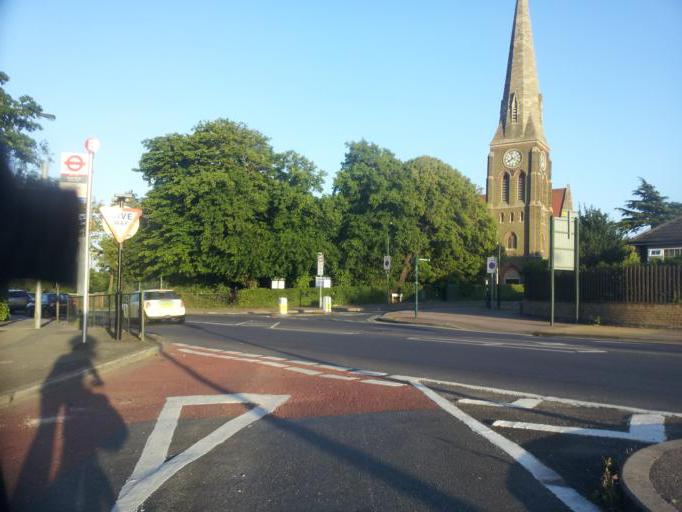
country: GB
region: England
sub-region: Greater London
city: Erith
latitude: 51.4805
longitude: 0.1759
